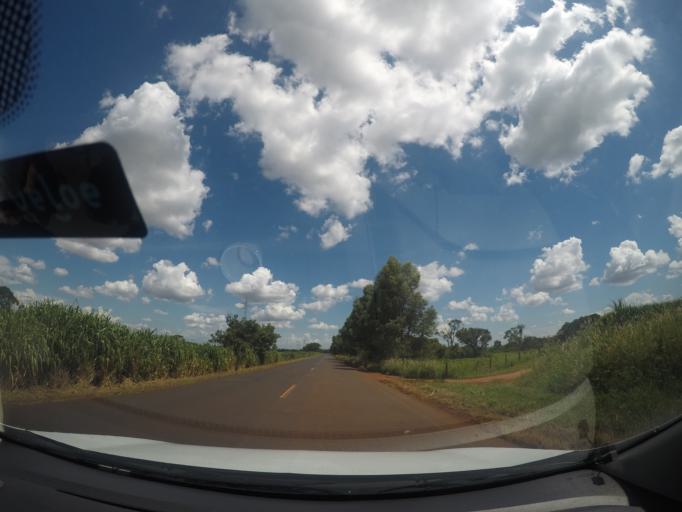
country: BR
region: Minas Gerais
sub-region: Frutal
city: Frutal
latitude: -19.8364
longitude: -48.7355
